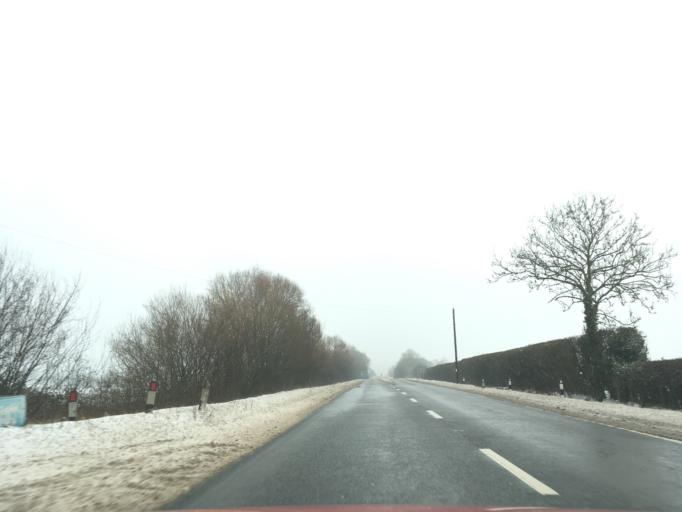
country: GB
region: England
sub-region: Worcestershire
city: Evesham
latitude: 52.0416
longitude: -1.9843
